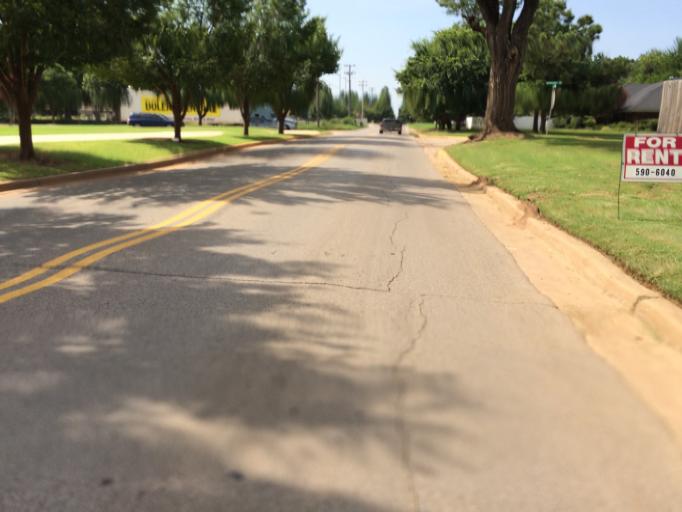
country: US
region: Oklahoma
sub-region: Cleveland County
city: Norman
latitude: 35.2003
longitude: -97.4502
